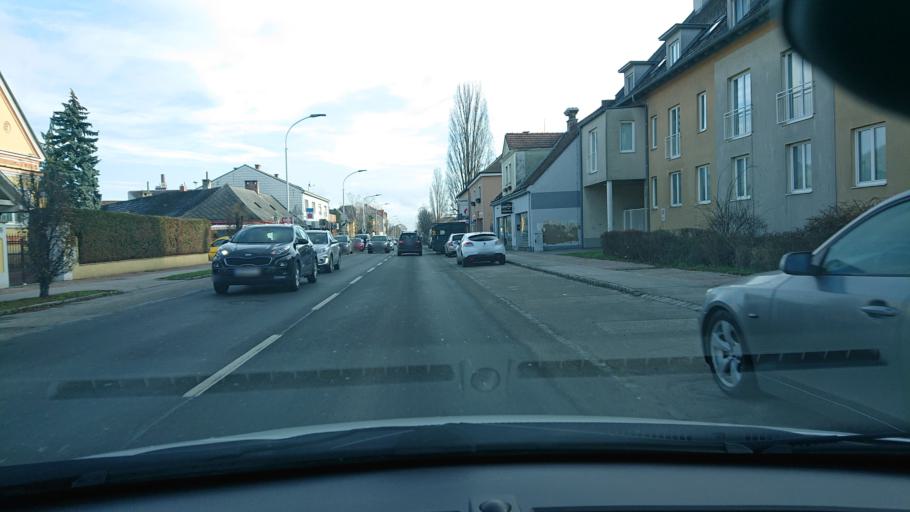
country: AT
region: Lower Austria
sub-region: Politischer Bezirk Baden
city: Hirtenberg
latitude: 47.9311
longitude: 16.1774
